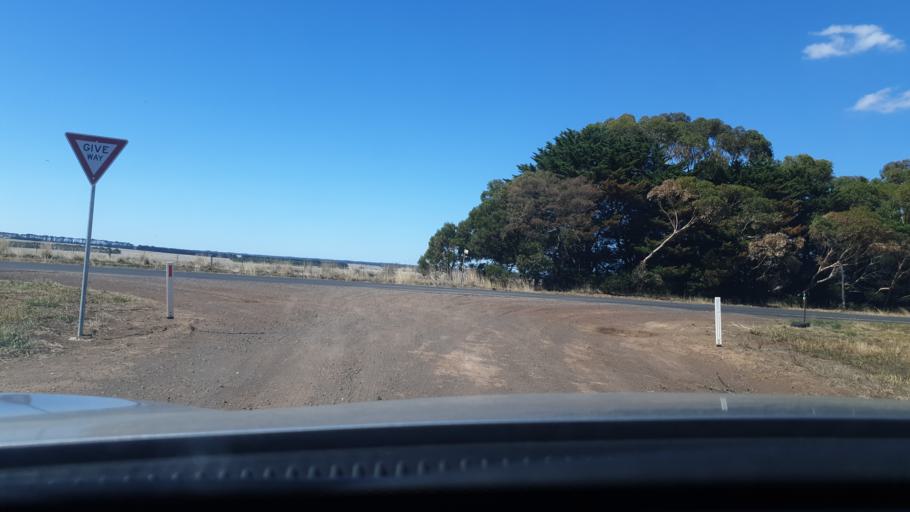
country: AU
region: Victoria
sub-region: Warrnambool
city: Warrnambool
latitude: -38.1647
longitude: 142.3966
